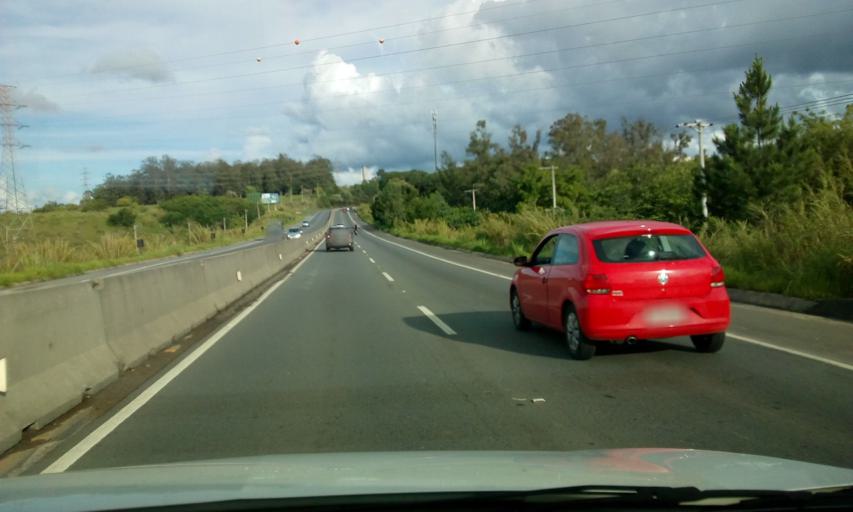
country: BR
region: Sao Paulo
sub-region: Itupeva
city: Itupeva
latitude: -23.1786
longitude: -46.9762
